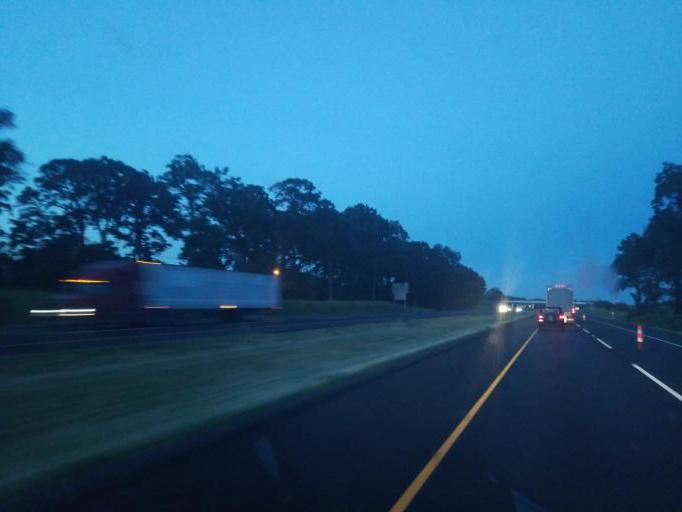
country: US
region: Indiana
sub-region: Saint Joseph County
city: Granger
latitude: 41.7337
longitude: -86.1158
